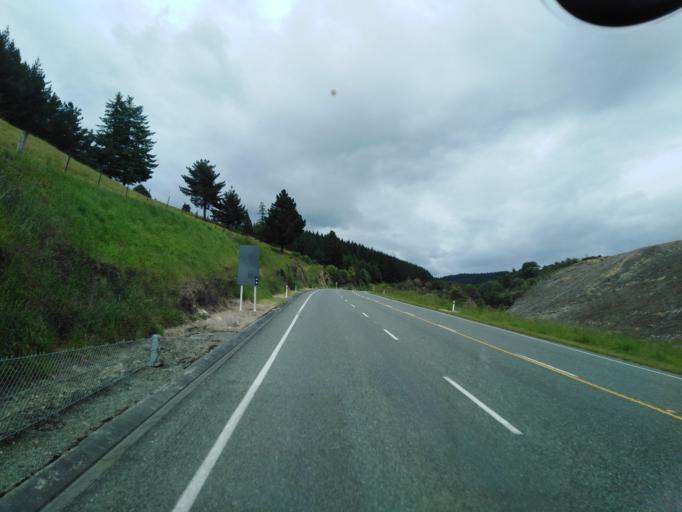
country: NZ
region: Tasman
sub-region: Tasman District
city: Wakefield
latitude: -41.4706
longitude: 172.9418
